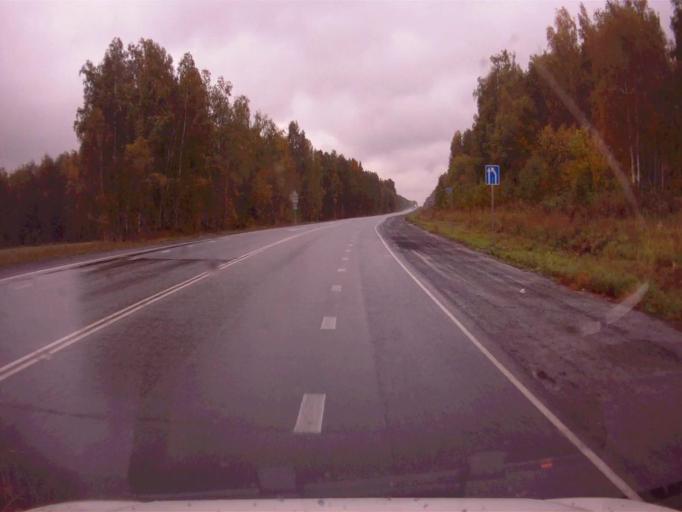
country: RU
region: Chelyabinsk
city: Roshchino
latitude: 55.3718
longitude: 61.1578
